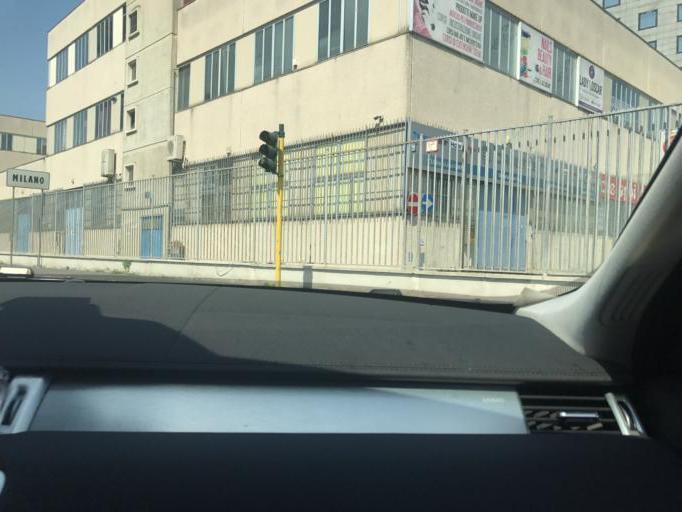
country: IT
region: Lombardy
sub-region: Citta metropolitana di Milano
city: Romano Banco
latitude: 45.4437
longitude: 9.1150
